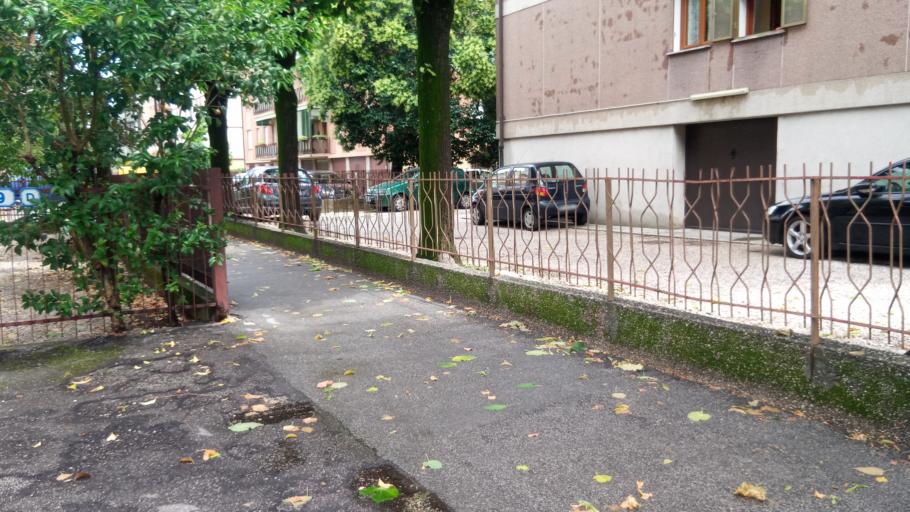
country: IT
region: Veneto
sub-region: Provincia di Padova
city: Padova
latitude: 45.4266
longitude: 11.8929
